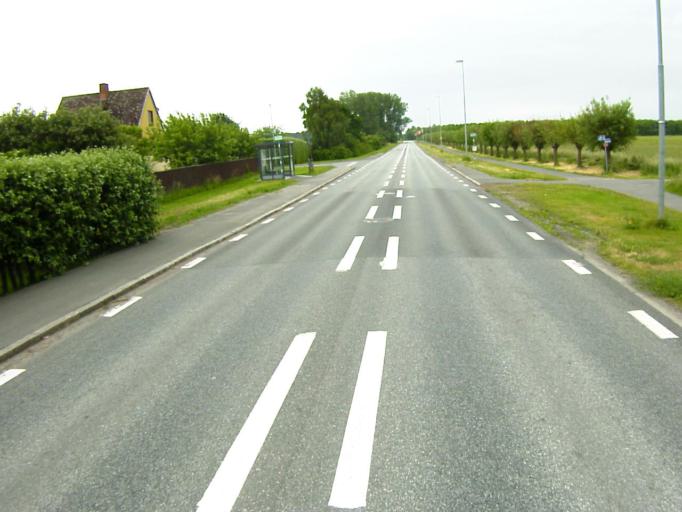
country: SE
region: Skane
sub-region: Kristianstads Kommun
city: Kristianstad
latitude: 56.0085
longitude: 14.1520
